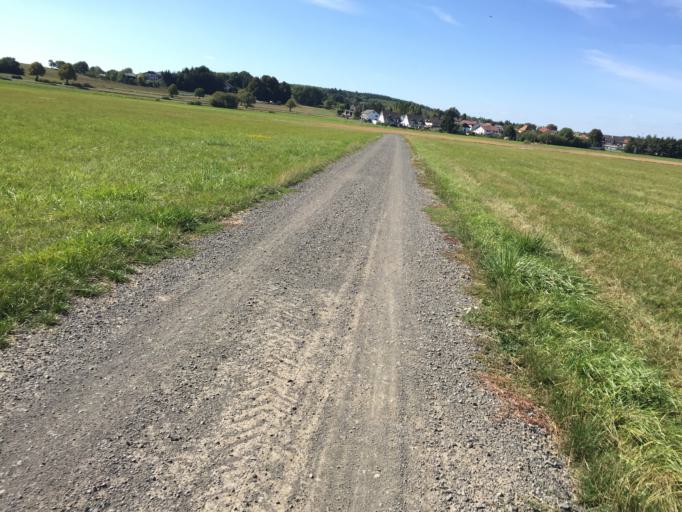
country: DE
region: Hesse
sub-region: Regierungsbezirk Giessen
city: Reiskirchen
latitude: 50.5906
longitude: 8.8654
